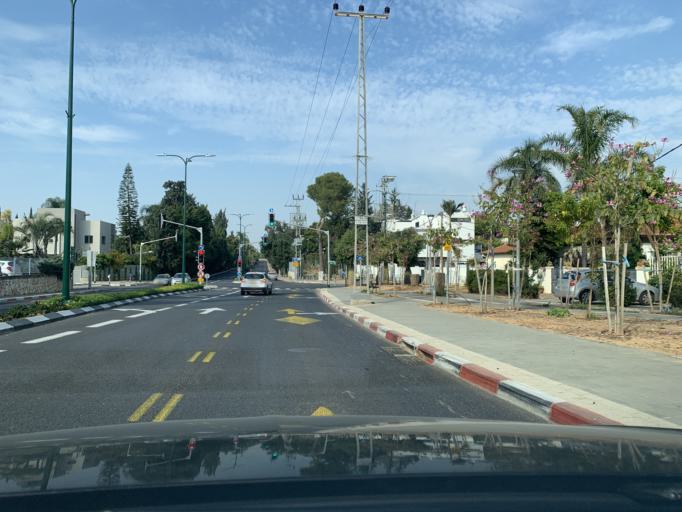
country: IL
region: Tel Aviv
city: Giv`at Shemu'el
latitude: 32.0581
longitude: 34.8497
